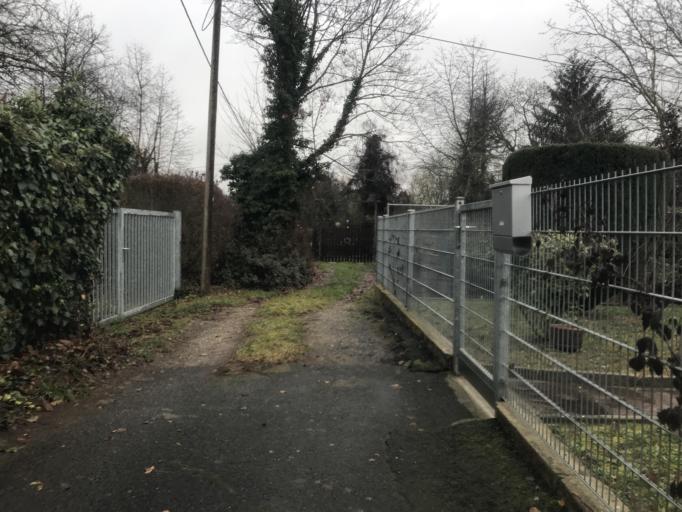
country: DE
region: Rheinland-Pfalz
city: Mainz
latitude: 50.0209
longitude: 8.2777
